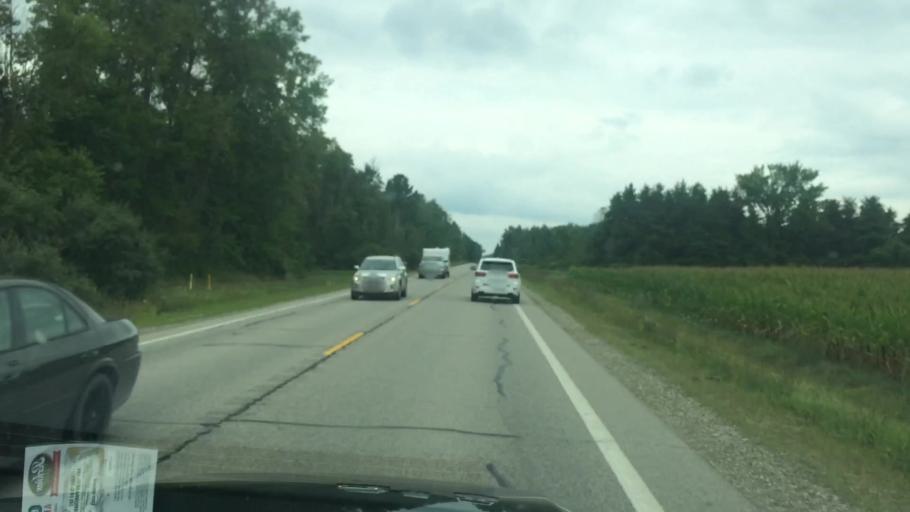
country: US
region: Michigan
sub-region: Tuscola County
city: Cass City
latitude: 43.4895
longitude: -83.0911
